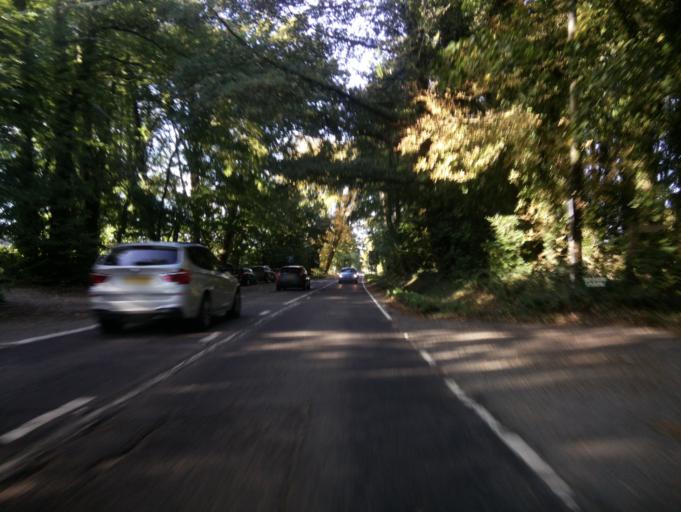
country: GB
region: England
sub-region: Hampshire
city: Alton
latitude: 51.1142
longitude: -0.9950
